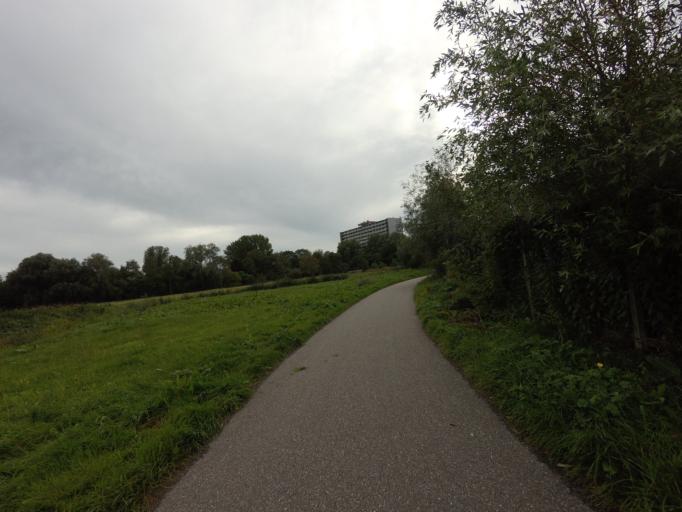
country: NL
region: Friesland
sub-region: Gemeente Leeuwarden
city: Bilgaard
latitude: 53.2192
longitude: 5.7933
